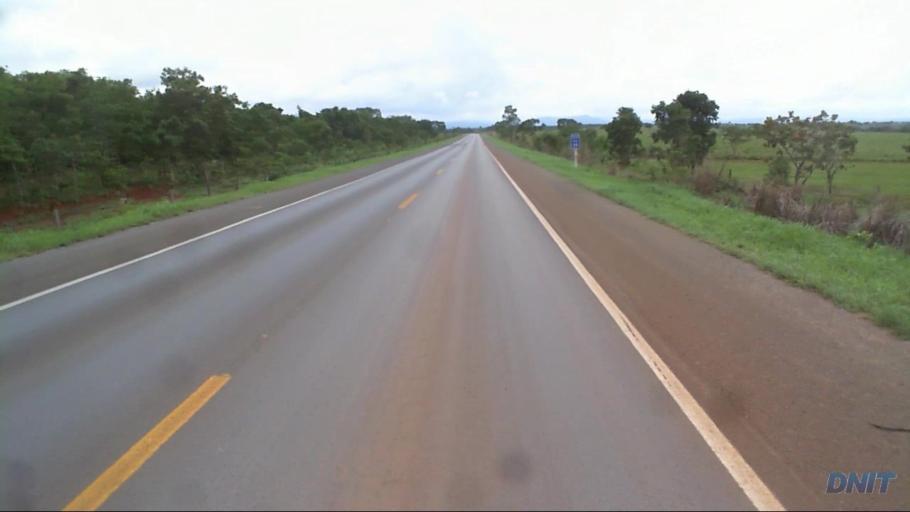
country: BR
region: Goias
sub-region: Padre Bernardo
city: Padre Bernardo
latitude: -15.1633
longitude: -48.3612
